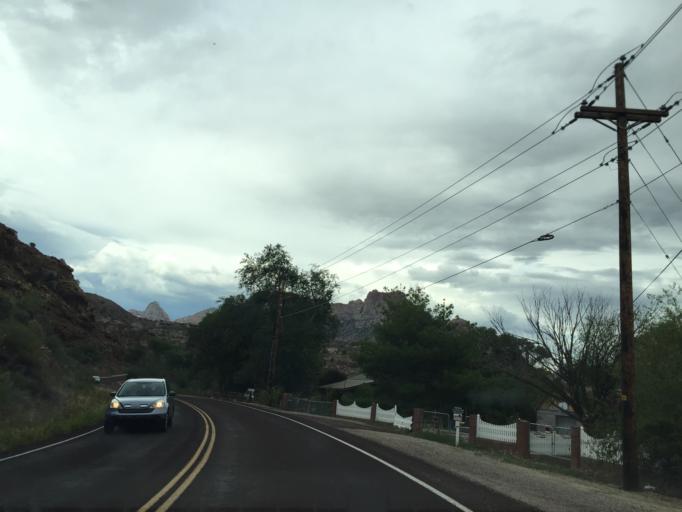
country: US
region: Utah
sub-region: Washington County
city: Hildale
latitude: 37.1603
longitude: -113.0291
